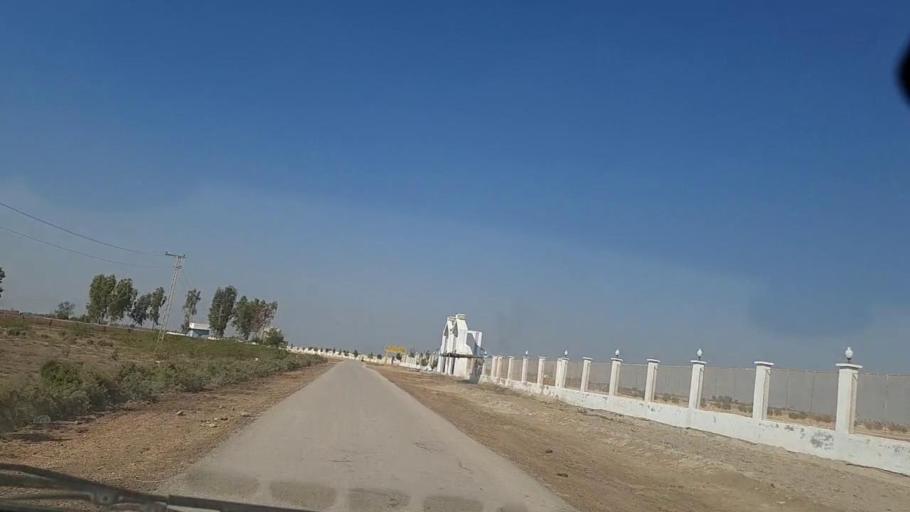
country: PK
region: Sindh
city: Mirpur Khas
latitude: 25.5167
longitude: 68.9494
